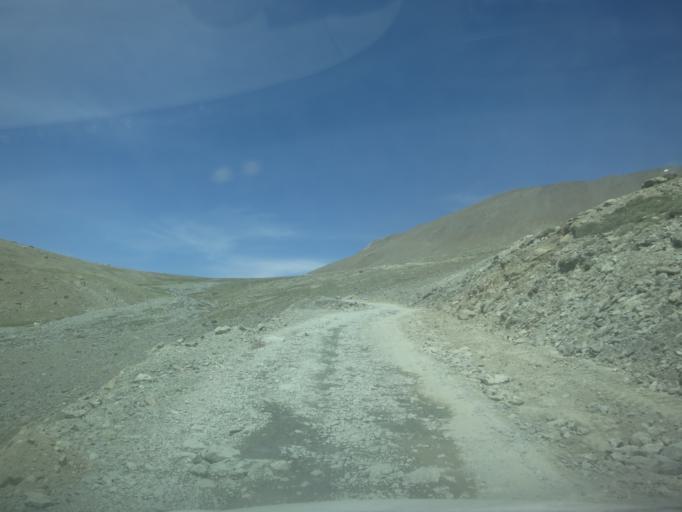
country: IN
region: Himachal Pradesh
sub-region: Kulu
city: Manali
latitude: 32.3883
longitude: 77.6270
